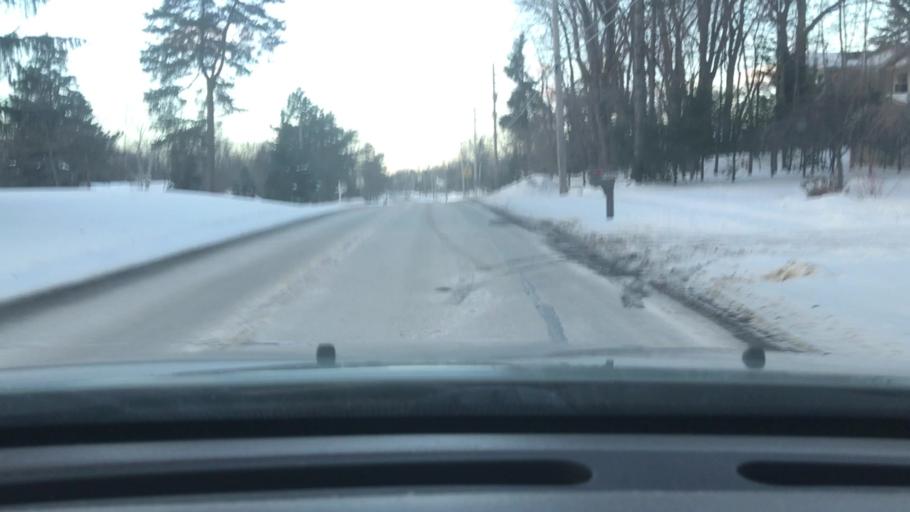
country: US
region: Ohio
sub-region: Lake County
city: Mentor
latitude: 41.6620
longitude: -81.3156
